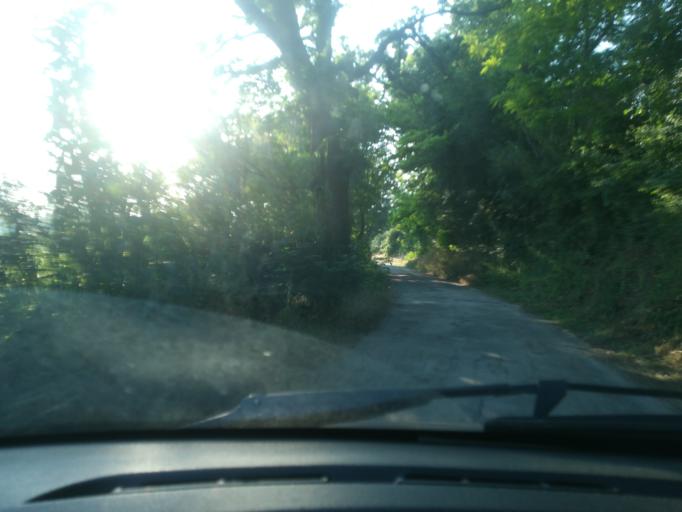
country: IT
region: The Marches
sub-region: Provincia di Macerata
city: Macerata
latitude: 43.2815
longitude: 13.4625
